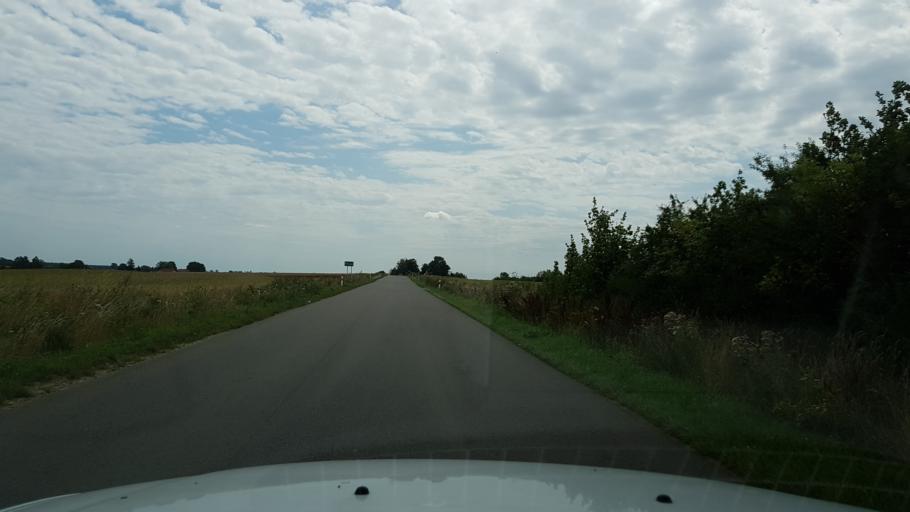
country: PL
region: West Pomeranian Voivodeship
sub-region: Powiat koszalinski
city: Mielno
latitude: 54.1720
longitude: 16.0078
